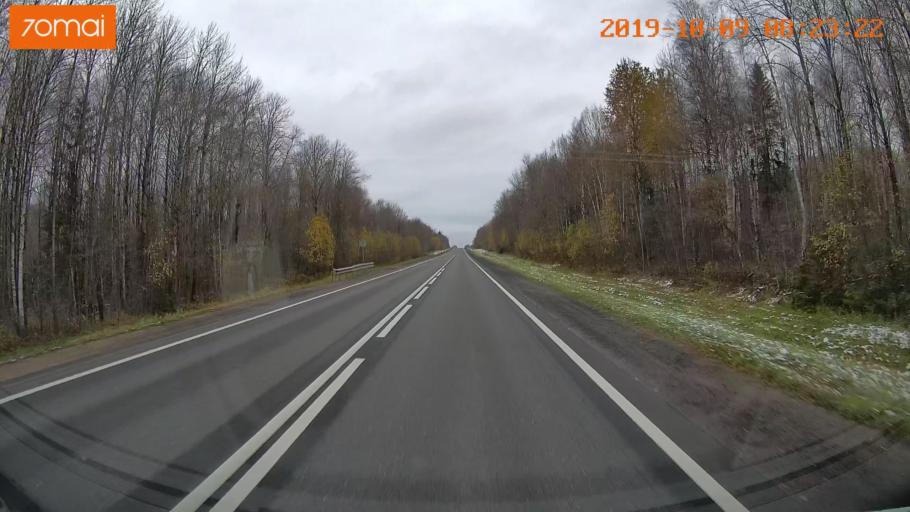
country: RU
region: Vologda
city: Gryazovets
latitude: 58.7534
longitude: 40.2838
